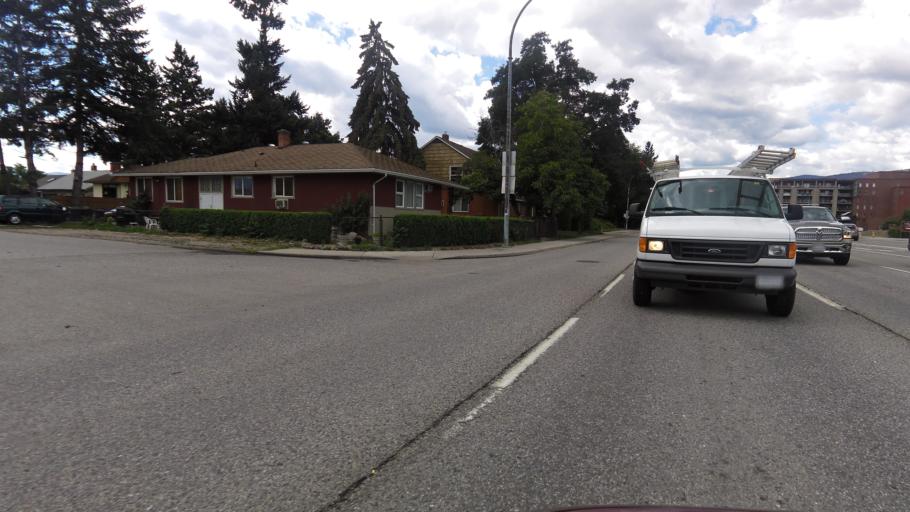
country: CA
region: British Columbia
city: Kelowna
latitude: 49.8835
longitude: -119.4779
